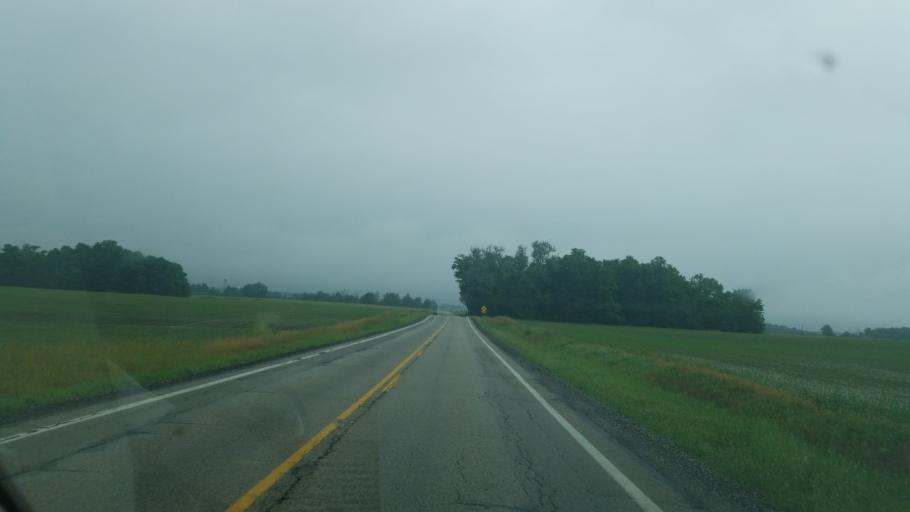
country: US
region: Ohio
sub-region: Crawford County
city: Bucyrus
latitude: 40.8702
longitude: -82.8550
